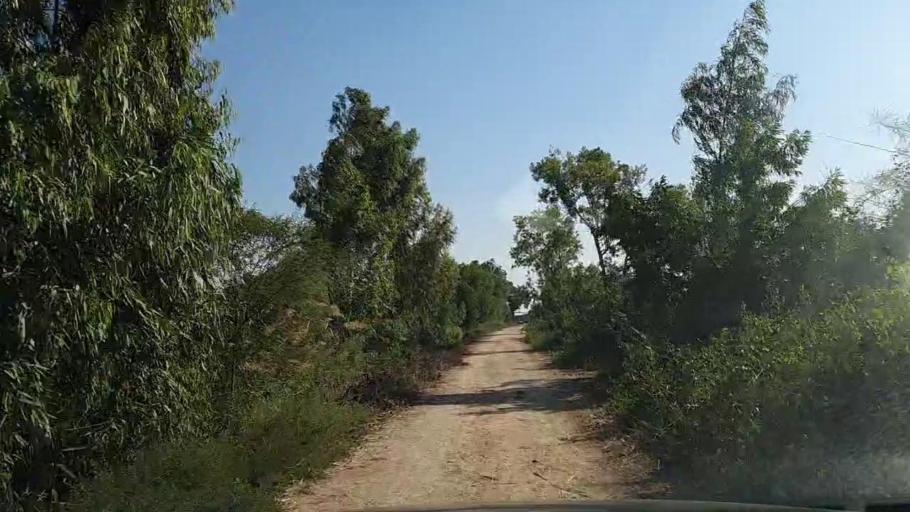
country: PK
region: Sindh
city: Mirpur Batoro
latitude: 24.7285
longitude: 68.2331
